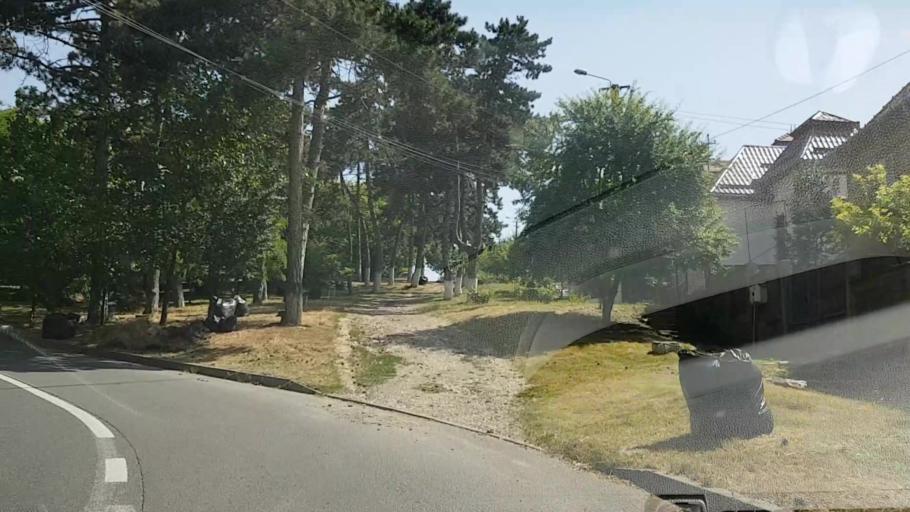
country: RO
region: Cluj
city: Turda
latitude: 46.5778
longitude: 23.7912
